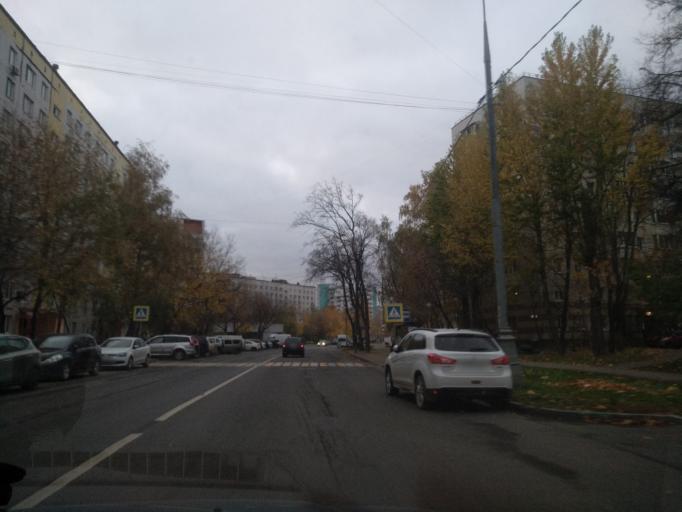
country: RU
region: Moscow
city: Kozeyevo
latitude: 55.8742
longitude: 37.6237
